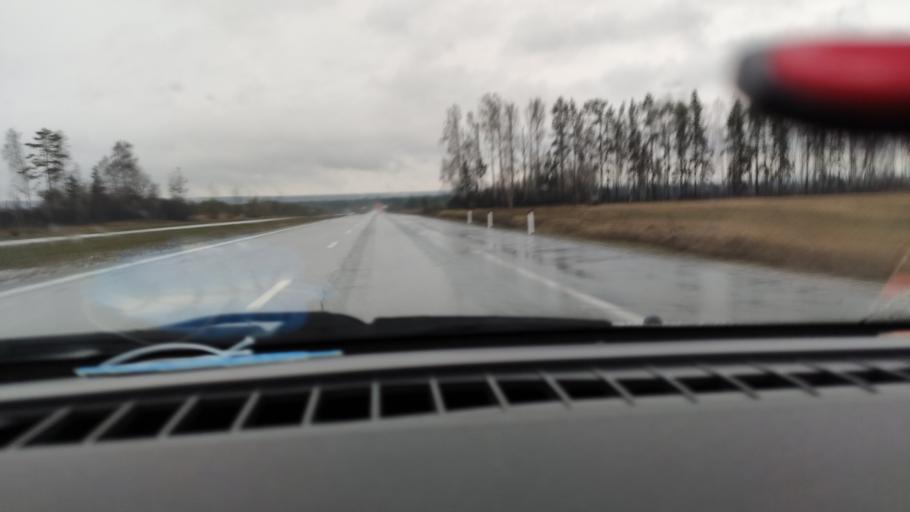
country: RU
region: Tatarstan
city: Yelabuga
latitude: 55.7835
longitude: 52.1723
